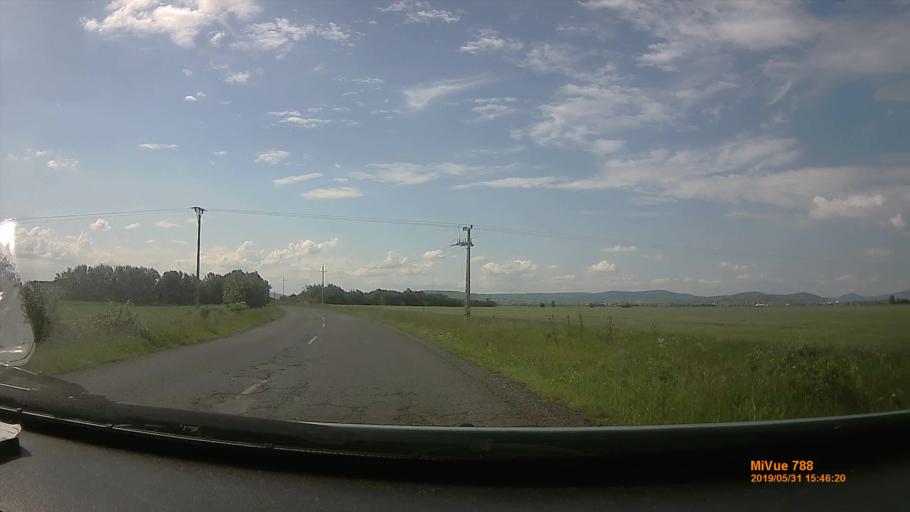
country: HU
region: Borsod-Abauj-Zemplen
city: Taktaszada
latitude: 48.1239
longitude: 21.2146
